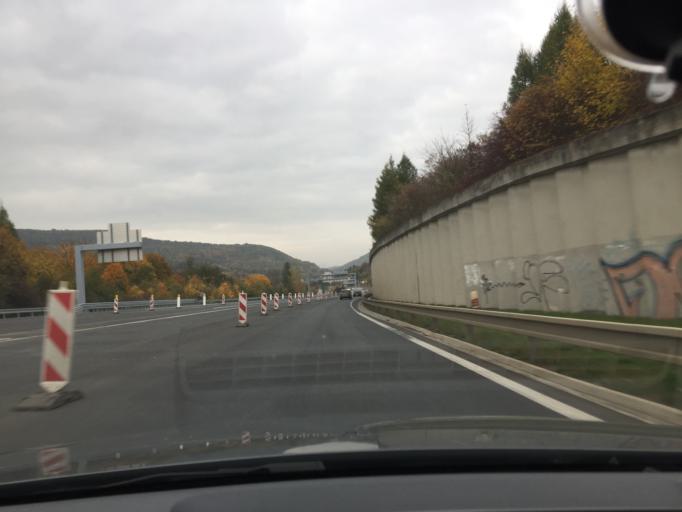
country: CZ
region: Ustecky
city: Rehlovice
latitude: 50.6131
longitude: 13.9643
